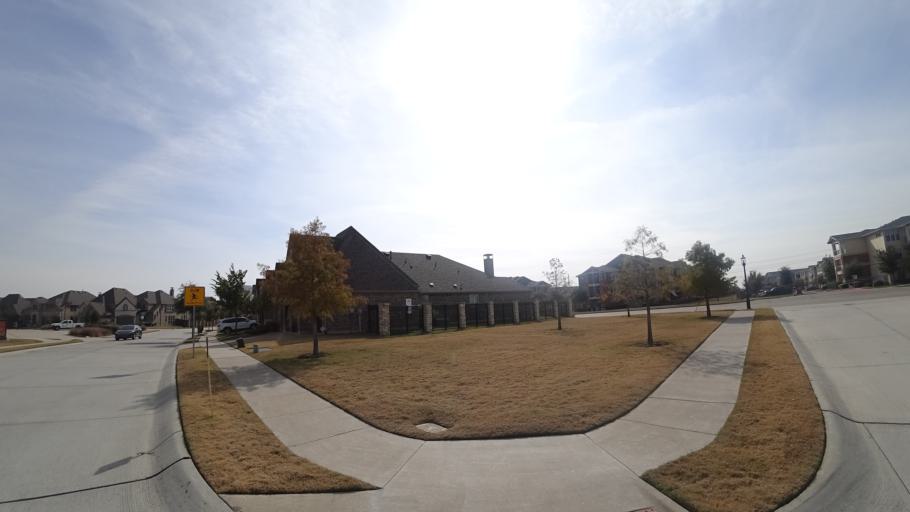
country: US
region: Texas
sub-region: Denton County
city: The Colony
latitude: 33.0641
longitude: -96.8805
